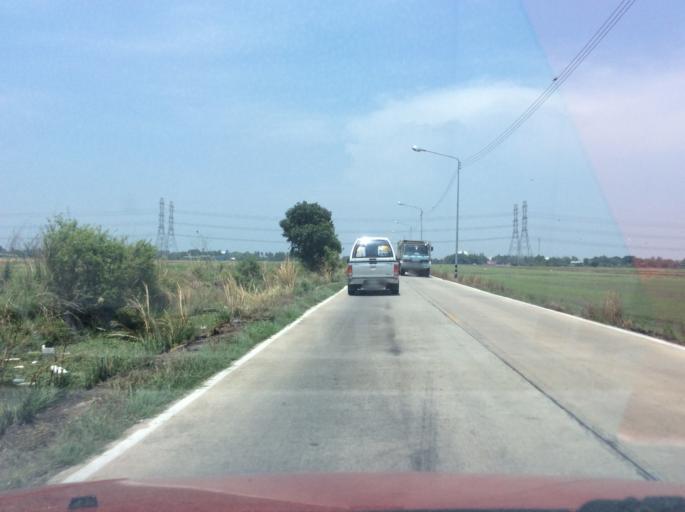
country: TH
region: Pathum Thani
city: Ban Lam Luk Ka
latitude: 13.9865
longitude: 100.7651
